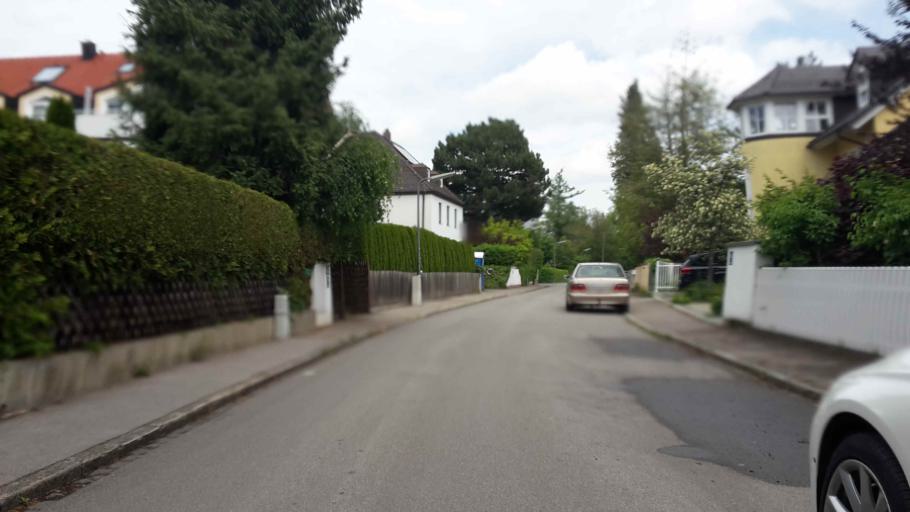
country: DE
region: Bavaria
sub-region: Upper Bavaria
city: Pasing
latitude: 48.1752
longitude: 11.4805
